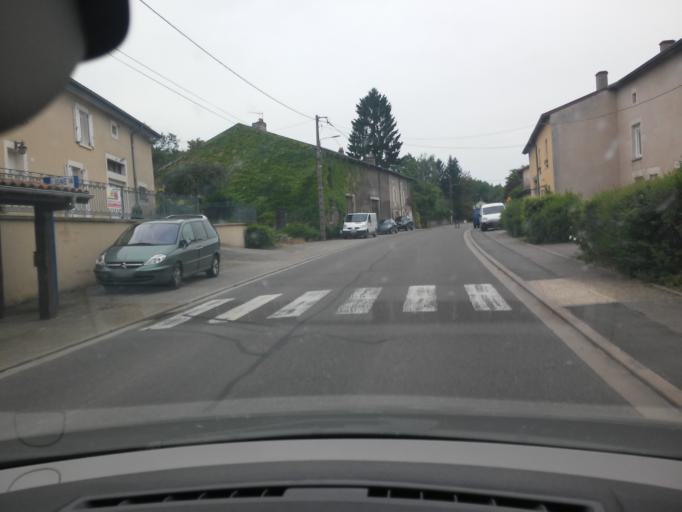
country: FR
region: Lorraine
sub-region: Departement de la Meuse
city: Lerouville
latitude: 48.8308
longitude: 5.5085
